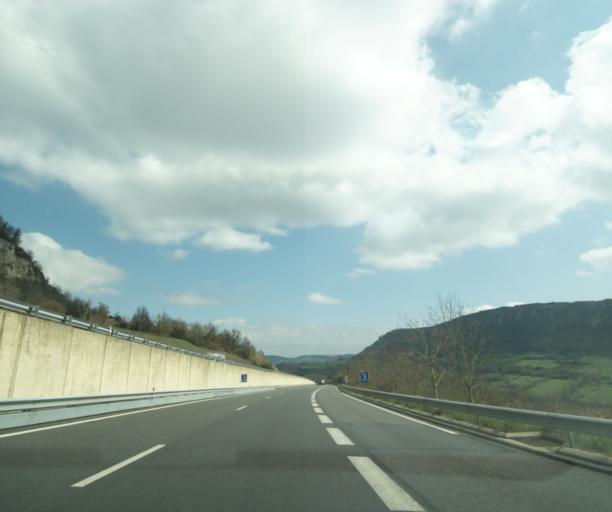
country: FR
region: Languedoc-Roussillon
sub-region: Departement de la Lozere
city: La Canourgue
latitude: 44.4142
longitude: 3.1780
